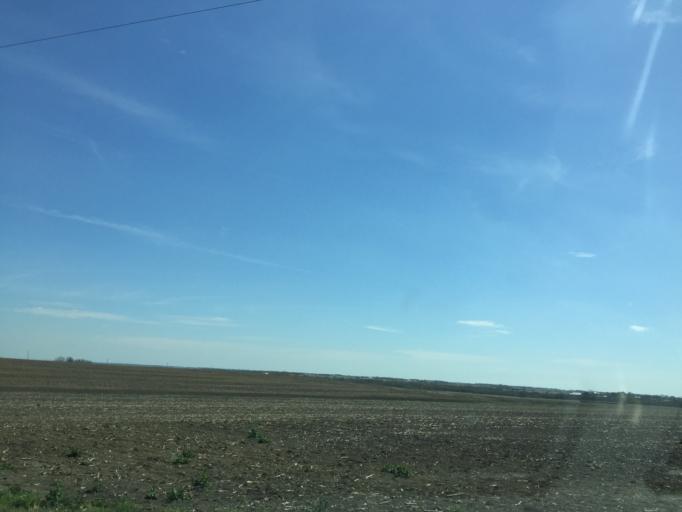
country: US
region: Texas
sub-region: Williamson County
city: Taylor
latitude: 30.5519
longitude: -97.3275
